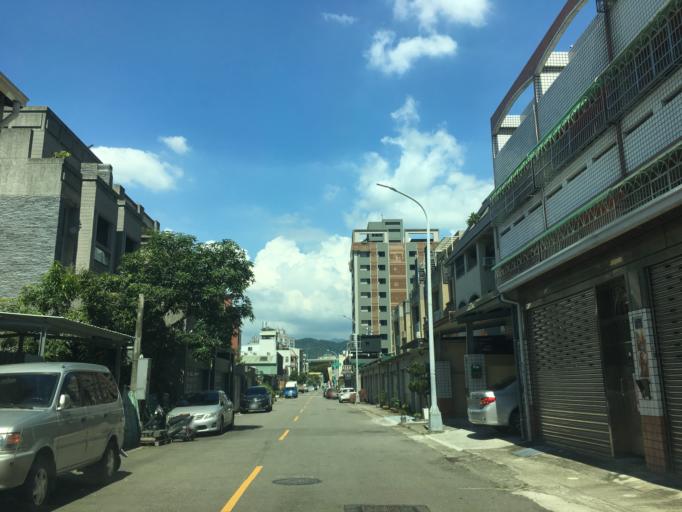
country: TW
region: Taiwan
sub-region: Taichung City
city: Taichung
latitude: 24.1450
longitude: 120.7080
